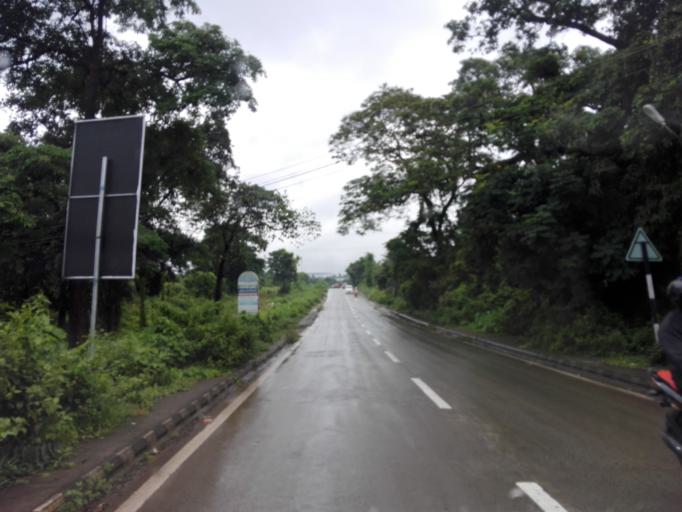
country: IN
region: Kerala
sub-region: Ernakulam
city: Aluva
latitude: 10.0502
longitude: 76.3461
